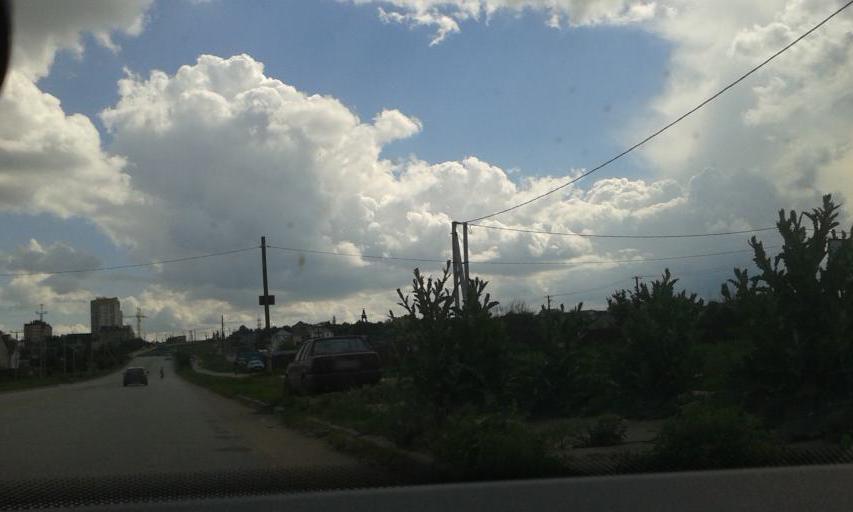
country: RU
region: Volgograd
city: Volgograd
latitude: 48.6538
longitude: 44.4128
